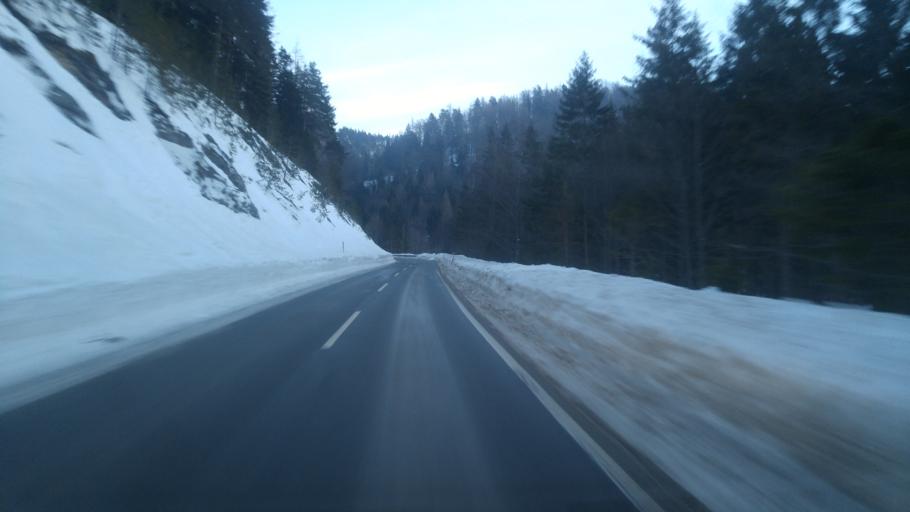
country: AT
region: Lower Austria
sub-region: Politischer Bezirk Wiener Neustadt
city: Rohr im Gebirge
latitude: 47.8687
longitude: 15.7928
